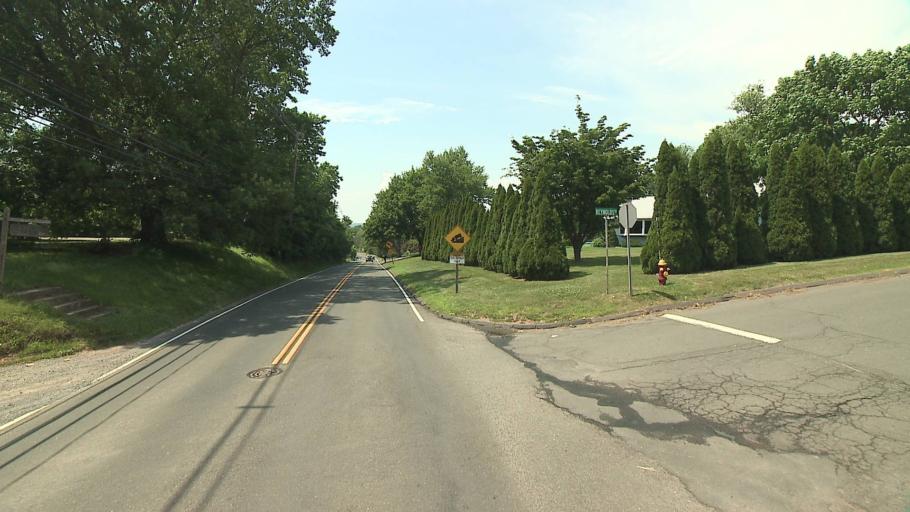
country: US
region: Connecticut
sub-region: New Haven County
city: Wallingford Center
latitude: 41.4460
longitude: -72.7943
